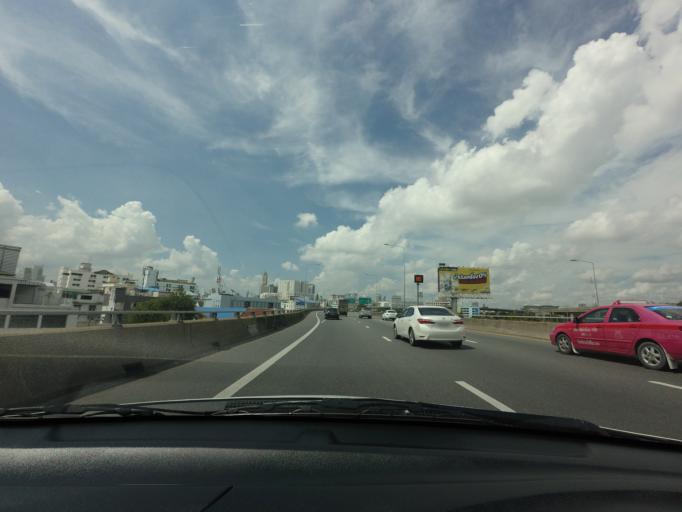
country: TH
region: Bangkok
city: Phaya Thai
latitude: 13.7764
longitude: 100.5328
